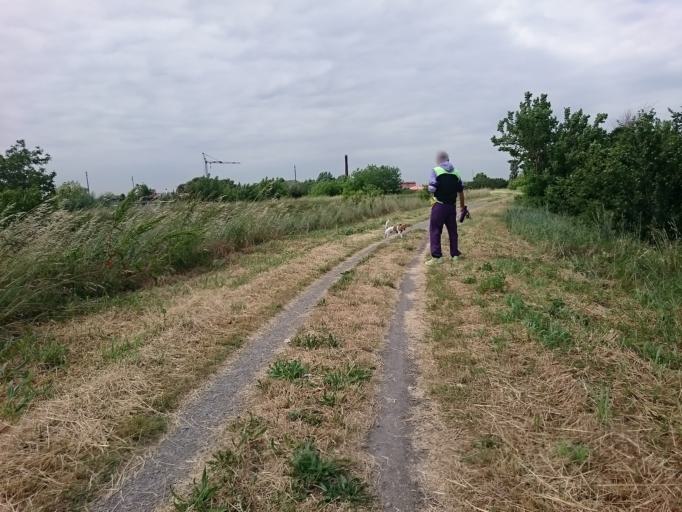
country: IT
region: Veneto
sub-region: Provincia di Padova
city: Este
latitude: 45.2223
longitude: 11.6788
